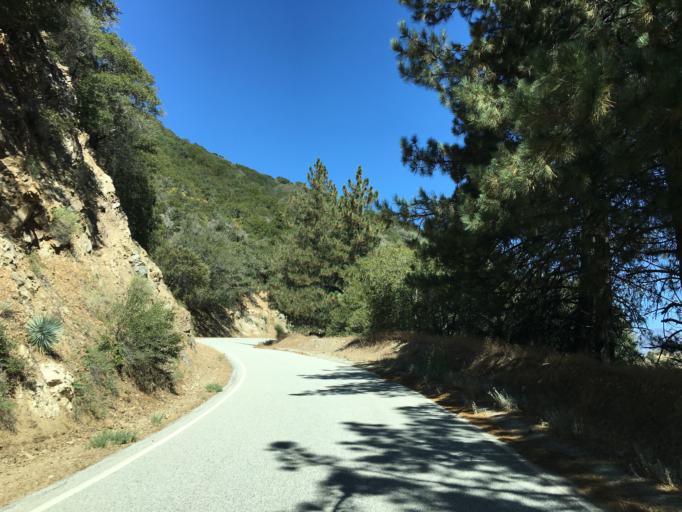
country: US
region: California
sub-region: San Bernardino County
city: San Antonio Heights
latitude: 34.2183
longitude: -117.6995
